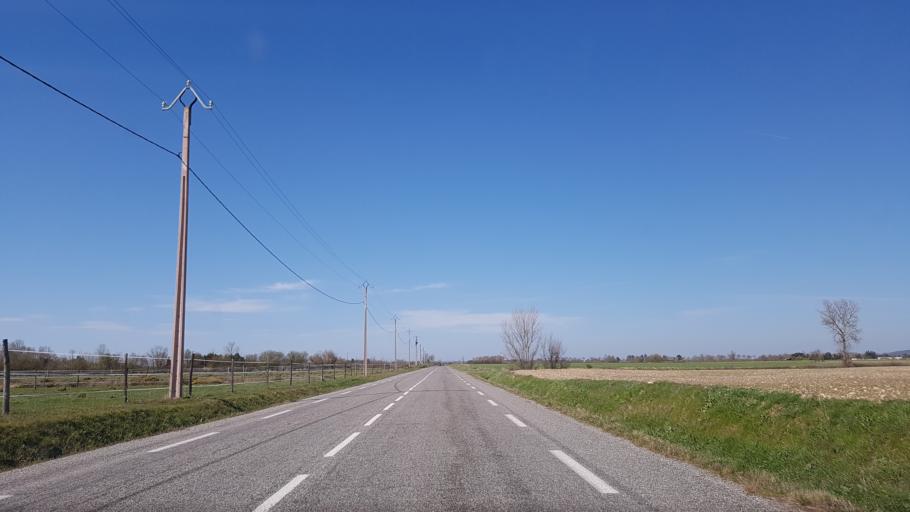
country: FR
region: Midi-Pyrenees
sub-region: Departement de l'Ariege
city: Mazeres
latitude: 43.2282
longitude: 1.6759
